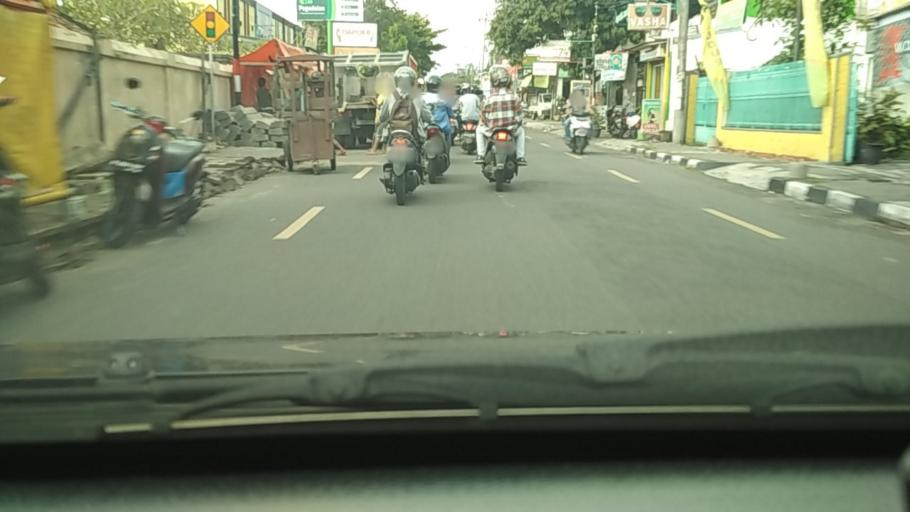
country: ID
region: Daerah Istimewa Yogyakarta
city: Yogyakarta
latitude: -7.7923
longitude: 110.3860
